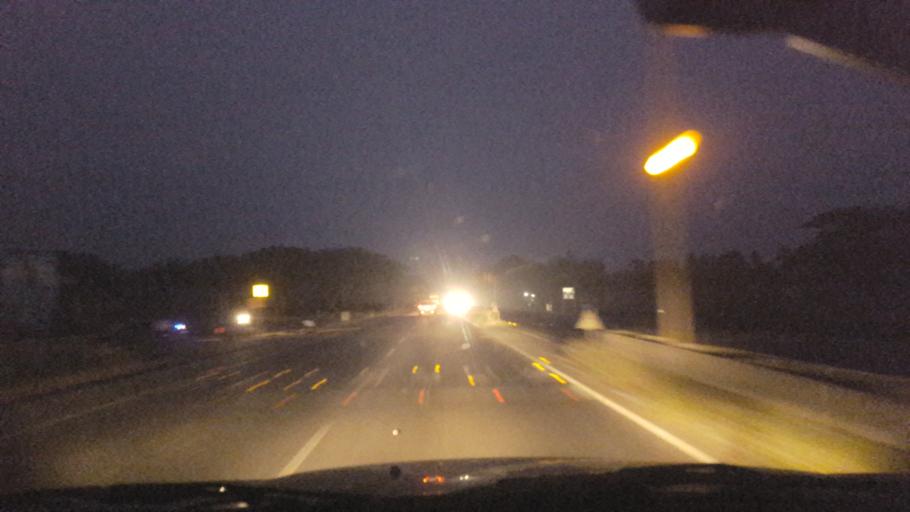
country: IN
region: Andhra Pradesh
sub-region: East Godavari
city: Peddapuram
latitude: 17.1377
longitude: 81.9620
